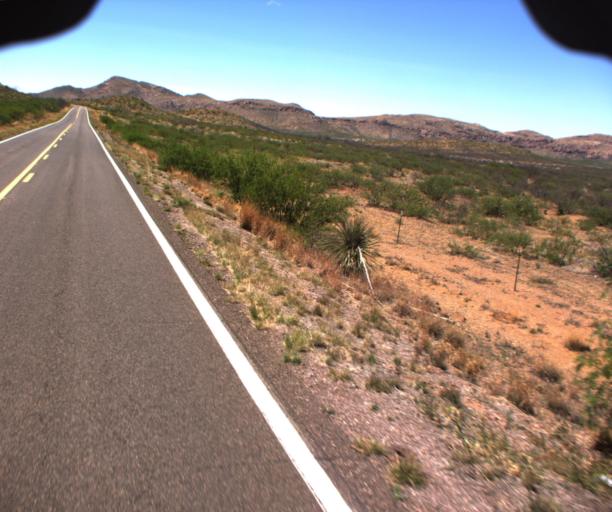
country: US
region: Arizona
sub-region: Cochise County
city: Douglas
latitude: 31.4888
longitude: -109.4347
